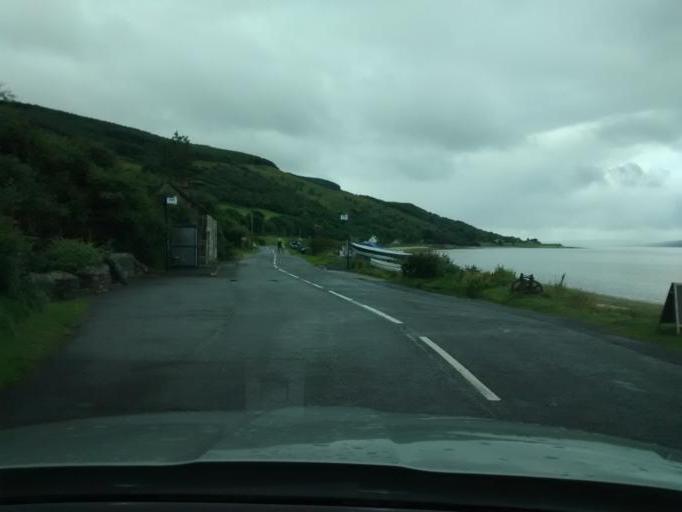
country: GB
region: Scotland
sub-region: North Ayrshire
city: Isle of Arran
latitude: 55.6440
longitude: -5.3830
